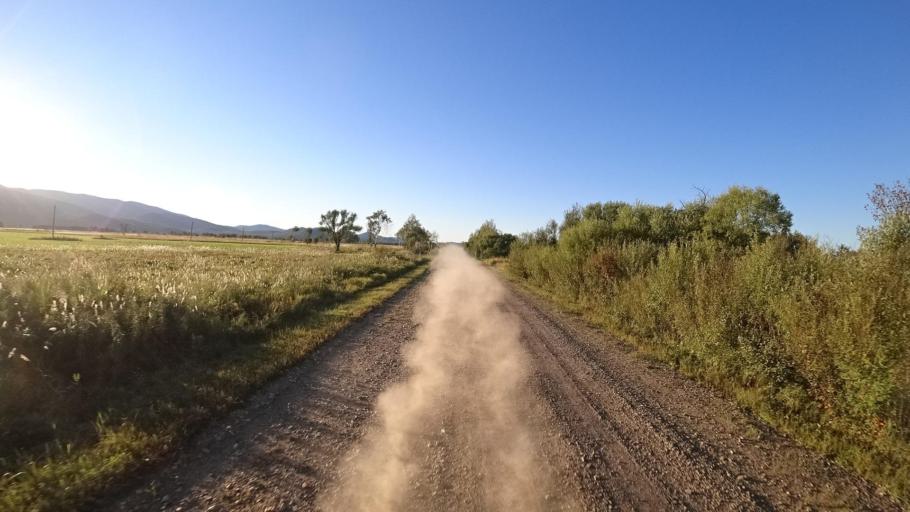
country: RU
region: Primorskiy
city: Kirovskiy
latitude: 44.8034
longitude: 133.6200
